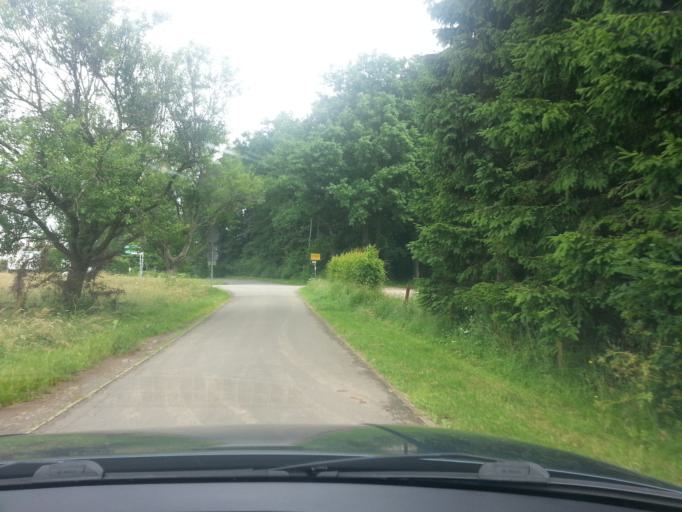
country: DE
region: Saarland
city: Marpingen
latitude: 49.4541
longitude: 7.0933
